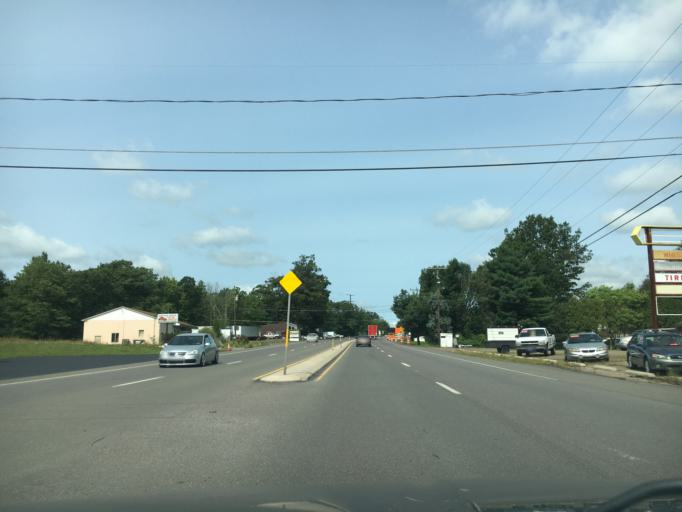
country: US
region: Pennsylvania
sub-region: Schuylkill County
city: Hometown
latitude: 40.8269
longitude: -75.9833
